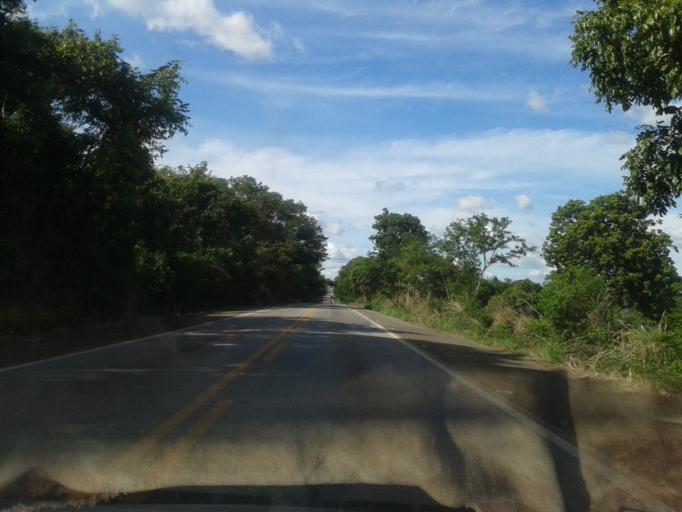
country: BR
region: Goias
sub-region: Mozarlandia
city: Mozarlandia
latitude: -14.9508
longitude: -50.5786
